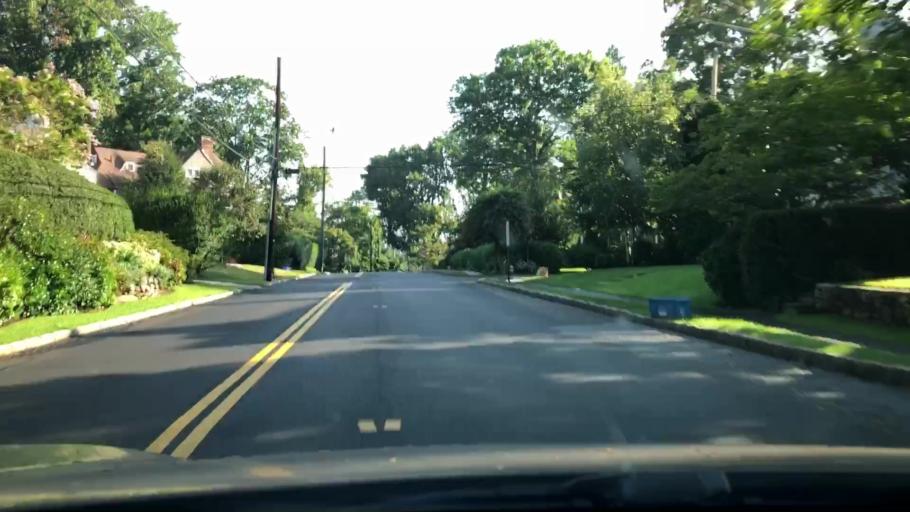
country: US
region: New York
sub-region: Westchester County
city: Bronxville
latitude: 40.9405
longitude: -73.8288
